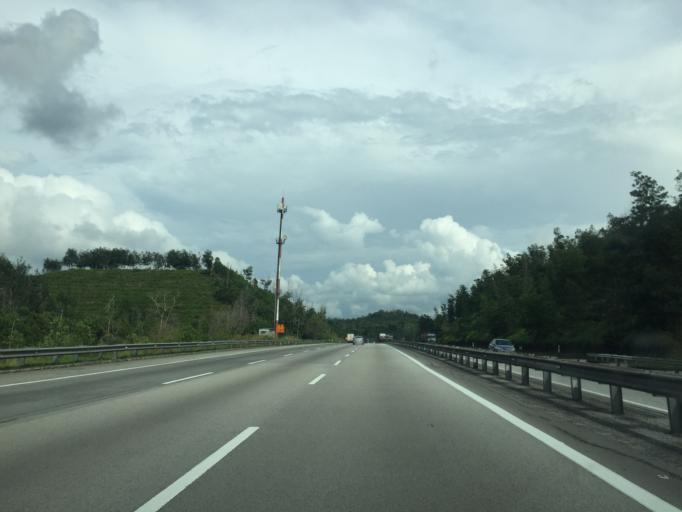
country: MY
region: Selangor
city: Batang Berjuntai
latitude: 3.5332
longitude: 101.5209
